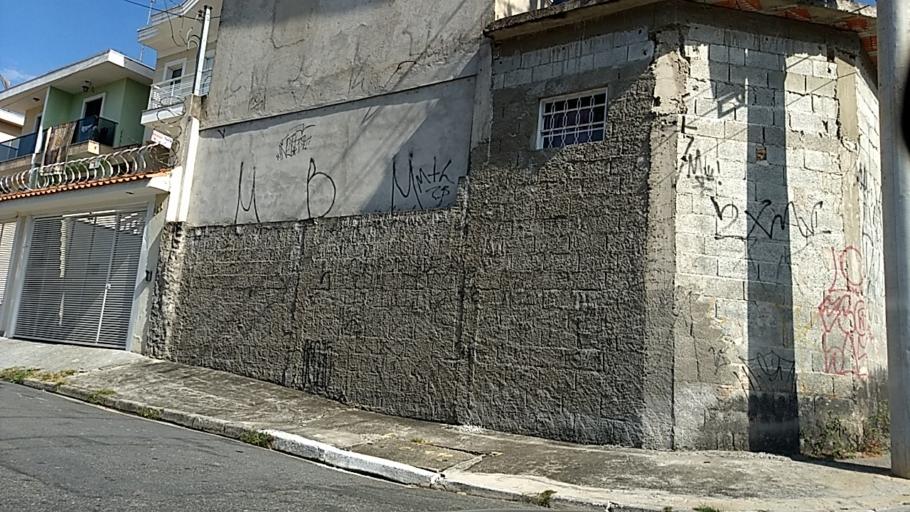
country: BR
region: Sao Paulo
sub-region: Guarulhos
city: Guarulhos
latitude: -23.4801
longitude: -46.5986
